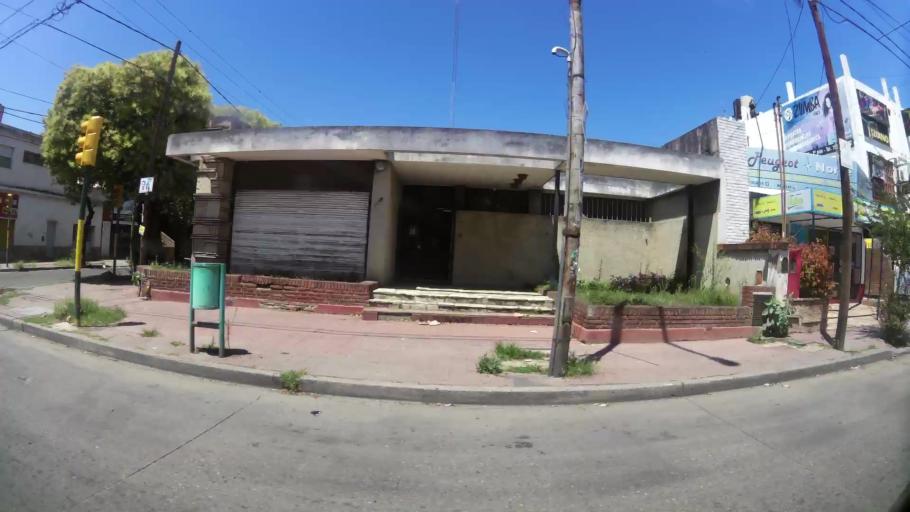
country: AR
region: Cordoba
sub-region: Departamento de Capital
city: Cordoba
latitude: -31.4145
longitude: -64.2209
